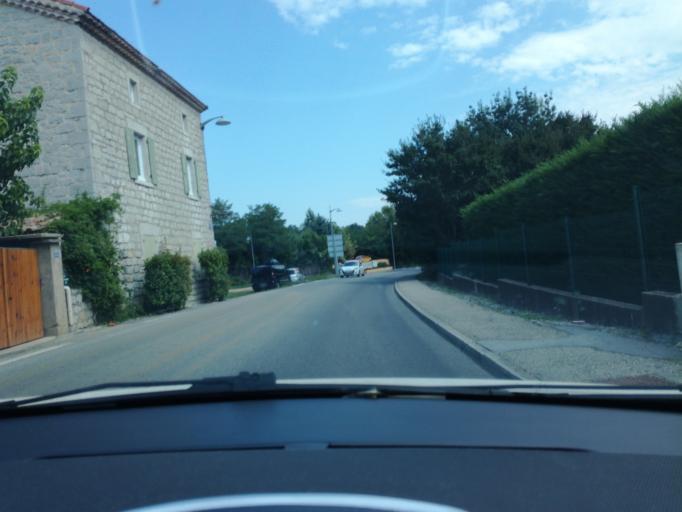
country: FR
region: Rhone-Alpes
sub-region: Departement de l'Ardeche
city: Ruoms
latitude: 44.4759
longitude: 4.3613
